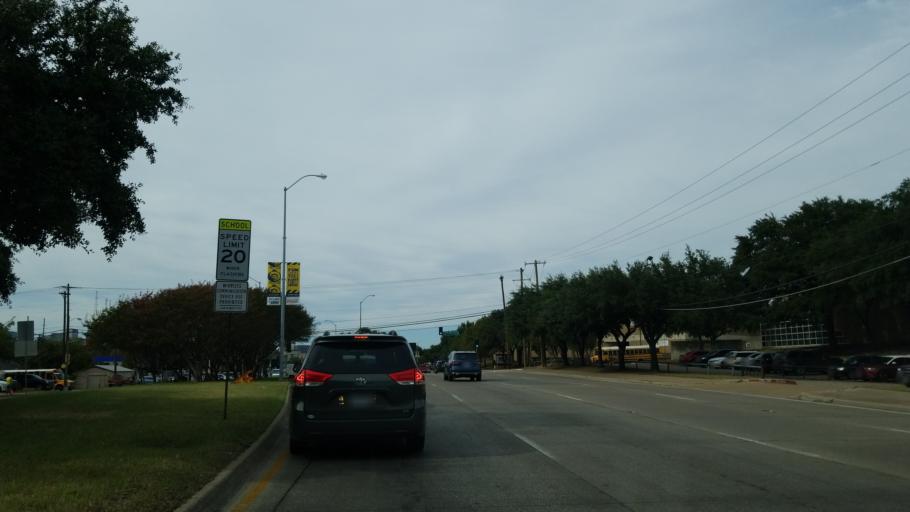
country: US
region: Texas
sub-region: Dallas County
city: Dallas
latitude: 32.7726
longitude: -96.7597
